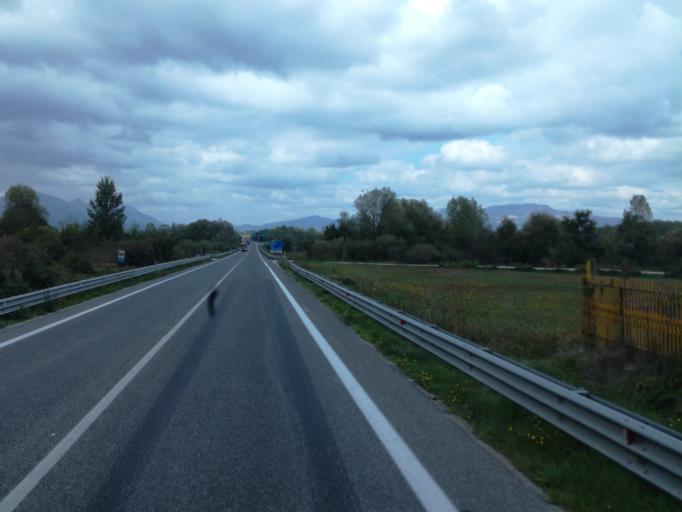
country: IT
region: Molise
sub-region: Provincia di Campobasso
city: San Polomatese
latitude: 41.4816
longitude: 14.4972
